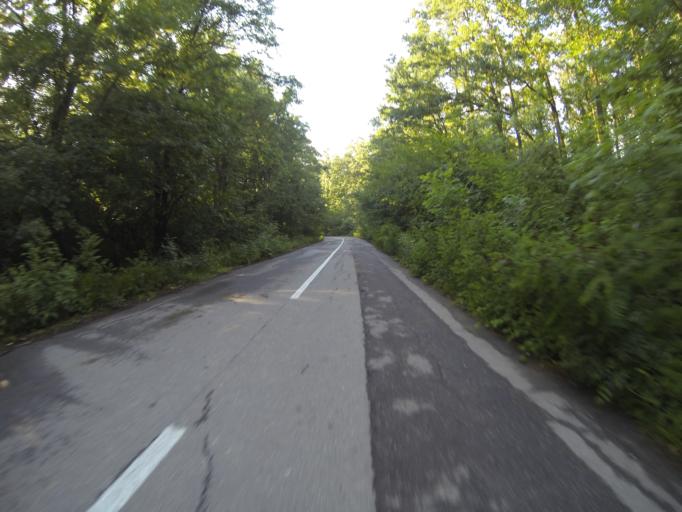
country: RO
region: Dolj
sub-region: Comuna Tuglui
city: Tuglui
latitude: 44.1675
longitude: 23.8257
